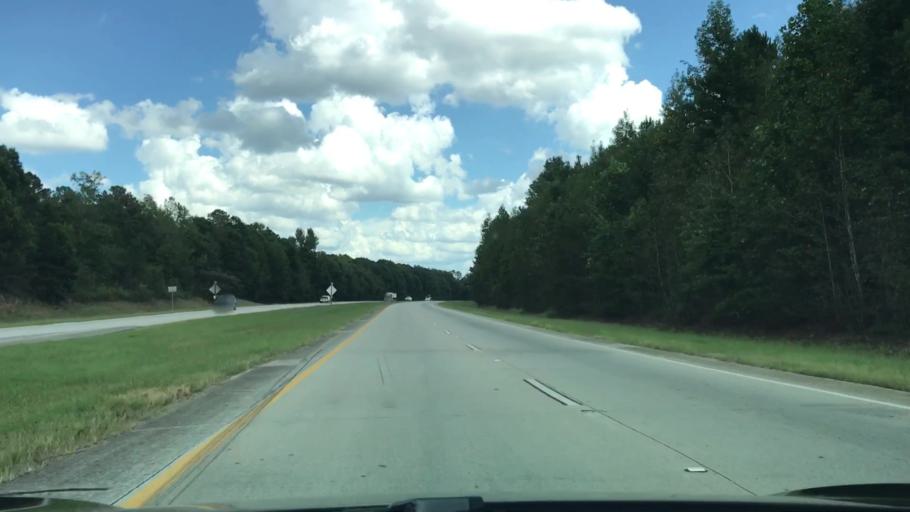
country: US
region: Georgia
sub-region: Oconee County
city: Bogart
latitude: 33.9172
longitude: -83.4810
